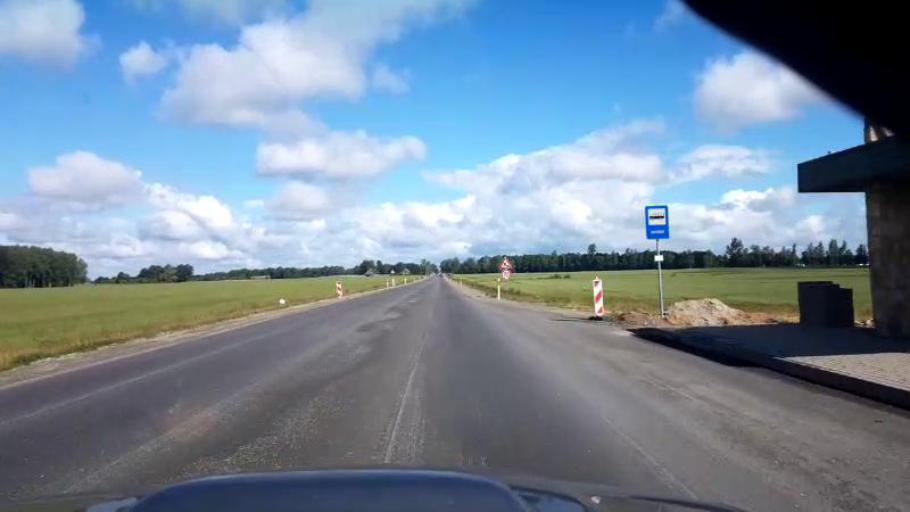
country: LV
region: Bauskas Rajons
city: Bauska
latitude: 56.3729
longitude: 24.2701
